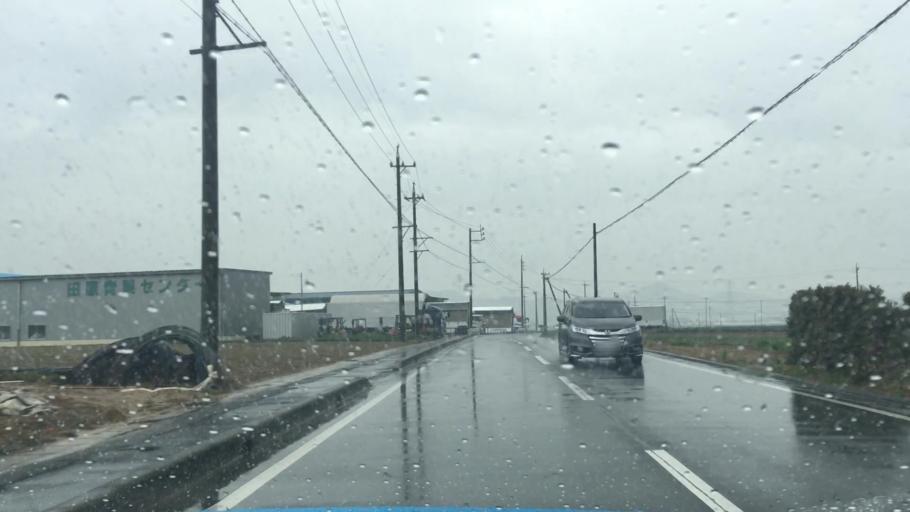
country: JP
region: Aichi
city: Tahara
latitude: 34.6476
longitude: 137.2958
